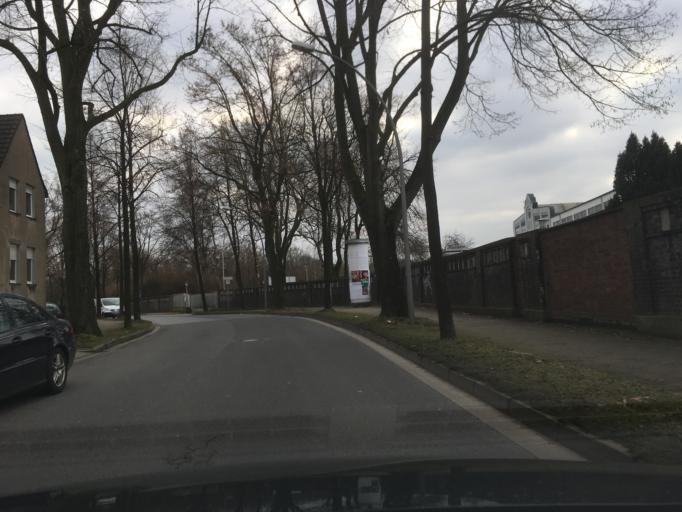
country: DE
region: North Rhine-Westphalia
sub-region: Regierungsbezirk Munster
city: Gladbeck
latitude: 51.5443
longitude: 7.0045
